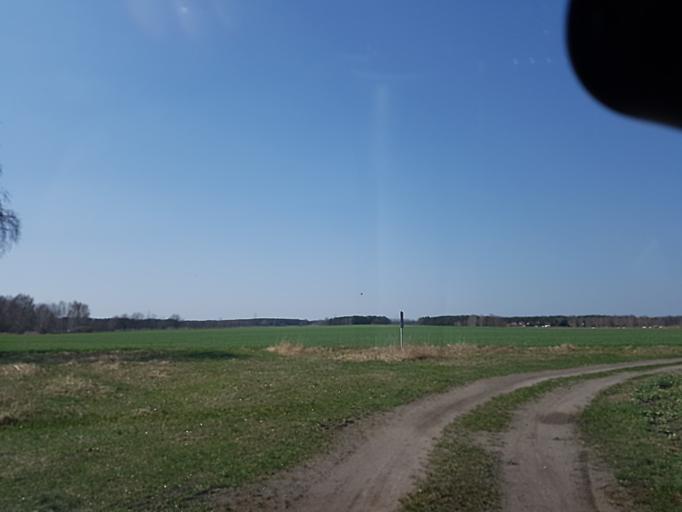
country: DE
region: Brandenburg
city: Trobitz
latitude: 51.5681
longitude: 13.4117
